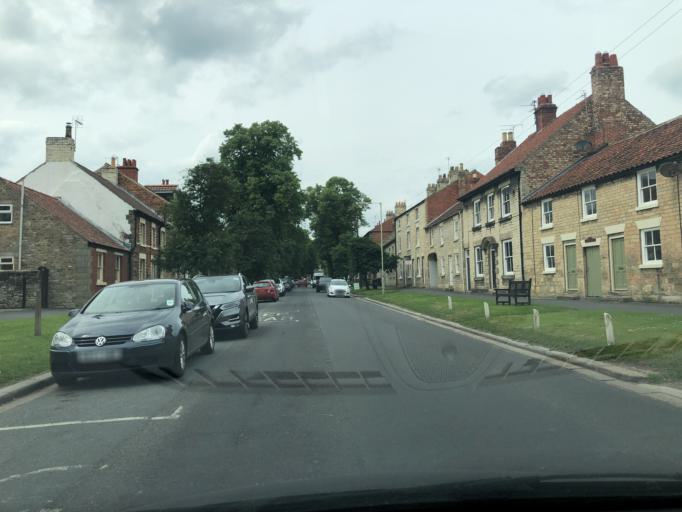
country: GB
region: England
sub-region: North Yorkshire
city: Pickering
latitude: 54.2421
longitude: -0.7709
